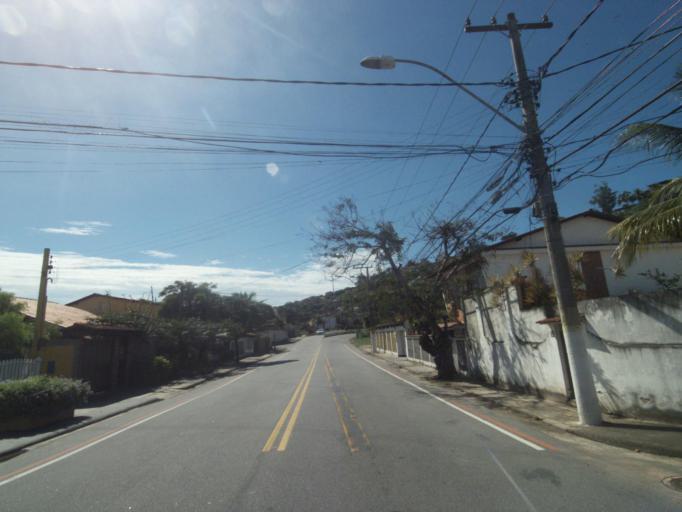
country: BR
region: Rio de Janeiro
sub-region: Niteroi
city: Niteroi
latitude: -22.9545
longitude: -43.0699
